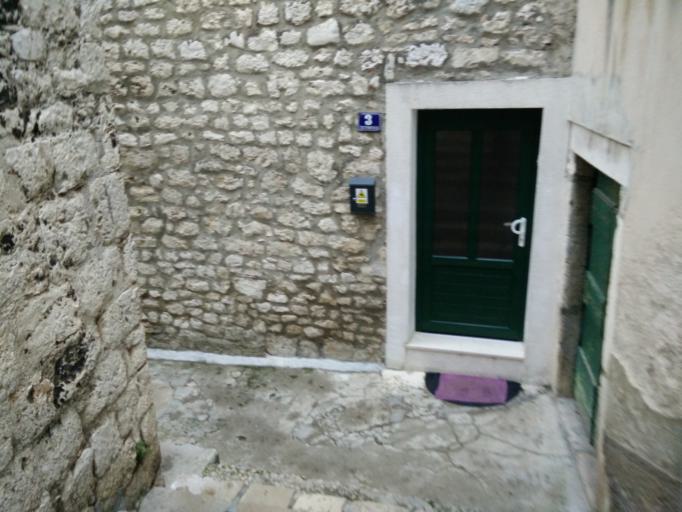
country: HR
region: Sibensko-Kniniska
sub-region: Grad Sibenik
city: Sibenik
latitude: 43.7383
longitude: 15.8883
